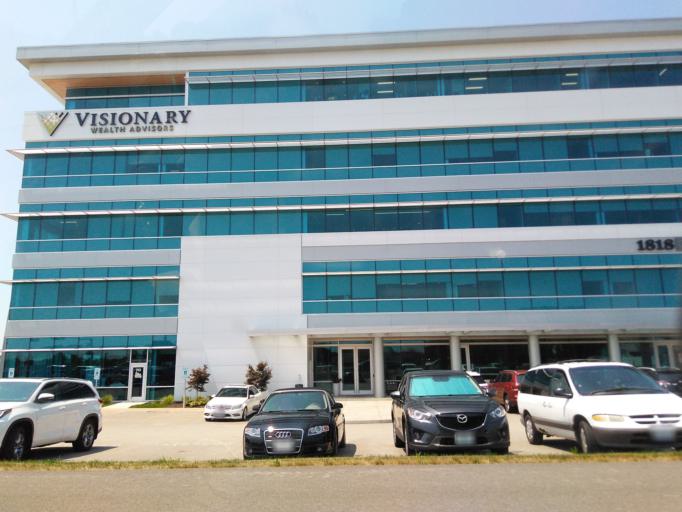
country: US
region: Illinois
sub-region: Saint Clair County
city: O'Fallon
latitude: 38.5803
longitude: -89.9291
